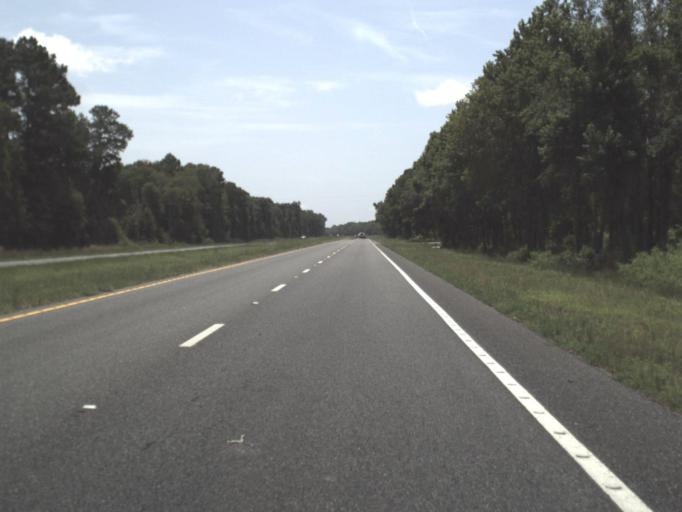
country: US
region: Florida
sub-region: Taylor County
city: Perry
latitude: 29.9716
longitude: -83.4808
